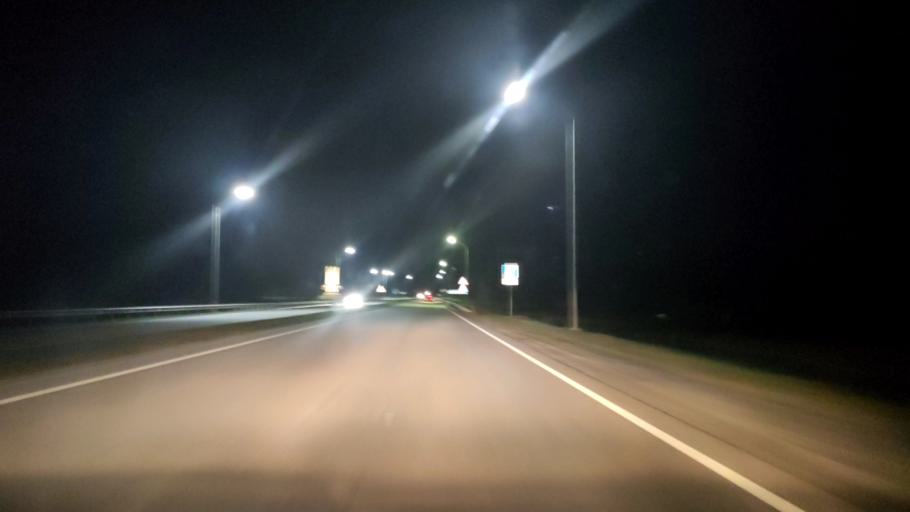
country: RU
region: Belgorod
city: Staryy Oskol
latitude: 51.4255
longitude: 37.8954
